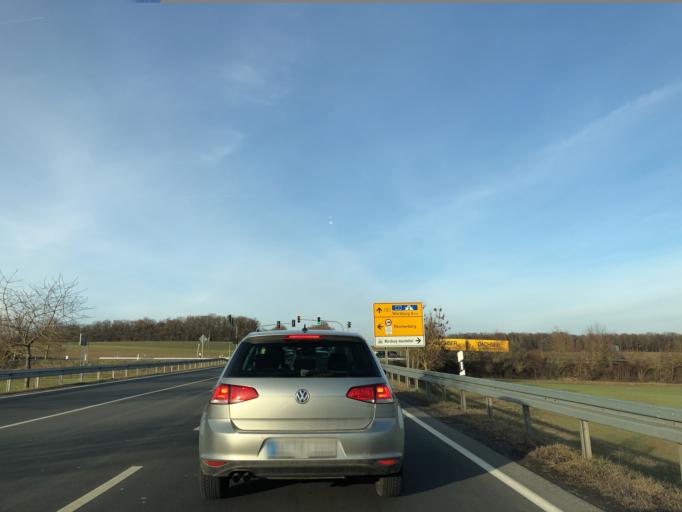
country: DE
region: Bavaria
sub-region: Regierungsbezirk Unterfranken
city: Reichenberg
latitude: 49.7309
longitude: 9.9334
